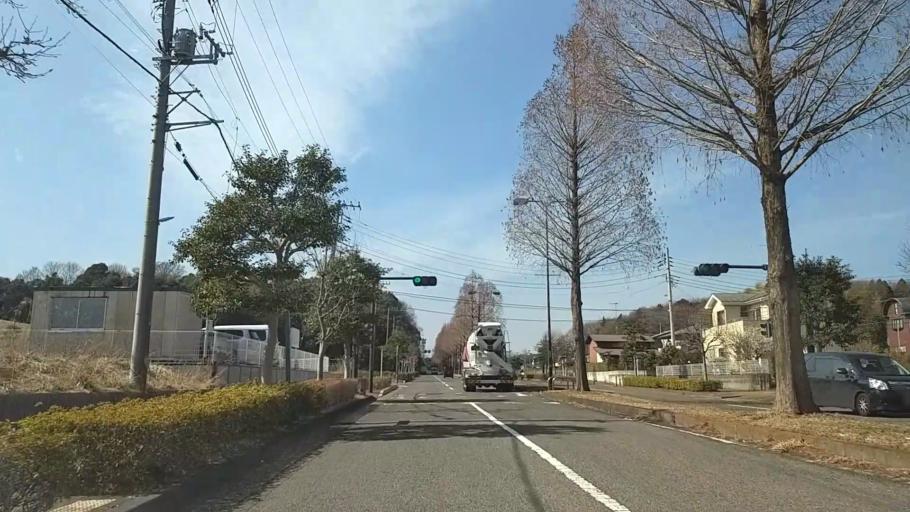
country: JP
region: Kanagawa
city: Fujisawa
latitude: 35.3906
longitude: 139.4298
